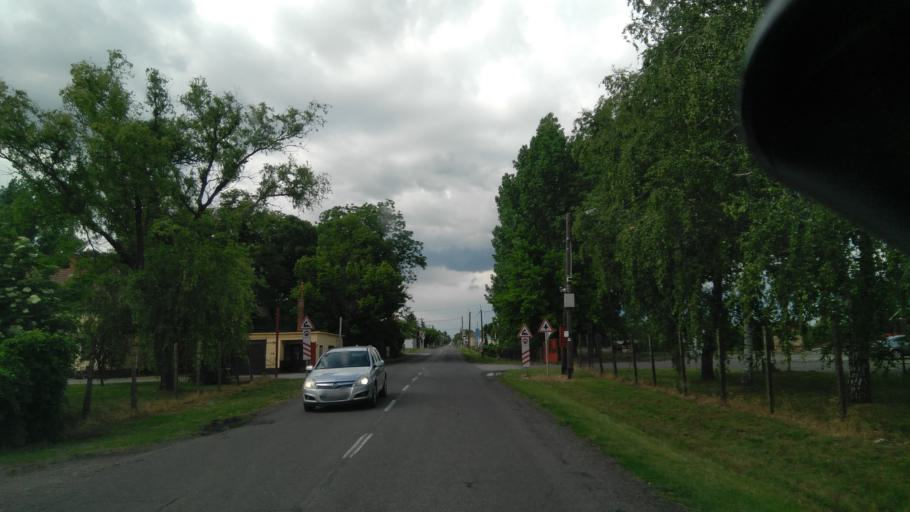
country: HU
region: Bekes
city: Gadoros
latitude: 46.6551
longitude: 20.5901
